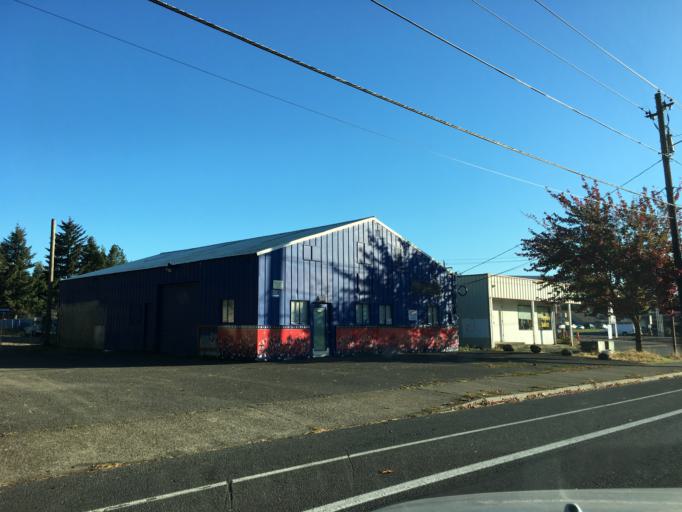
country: US
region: Oregon
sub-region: Multnomah County
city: Gresham
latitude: 45.5048
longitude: -122.4012
